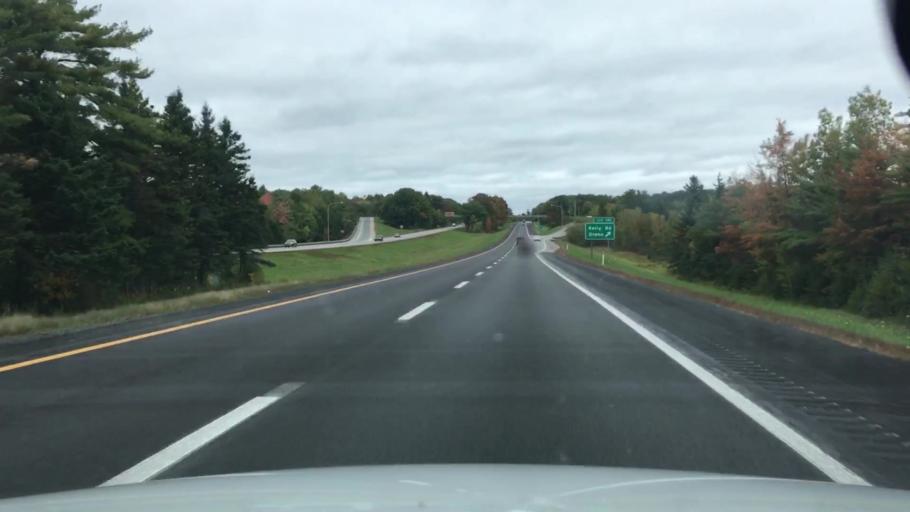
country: US
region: Maine
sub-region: Penobscot County
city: Veazie
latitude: 44.8679
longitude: -68.7063
